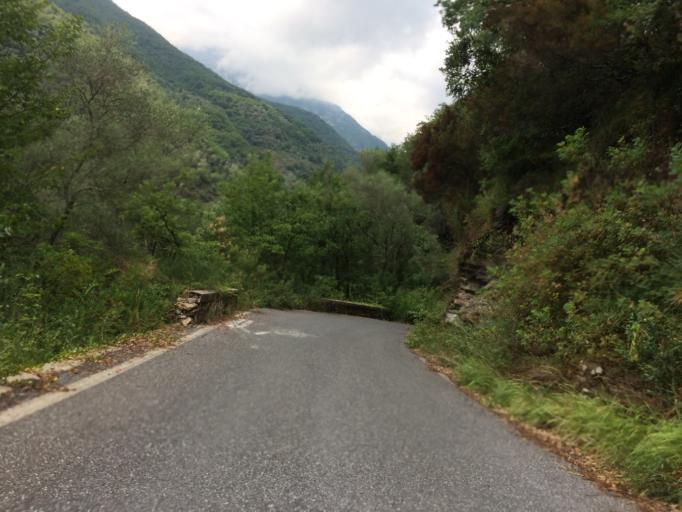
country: IT
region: Liguria
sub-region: Provincia di Imperia
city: Castel Vittorio
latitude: 43.9396
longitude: 7.6862
